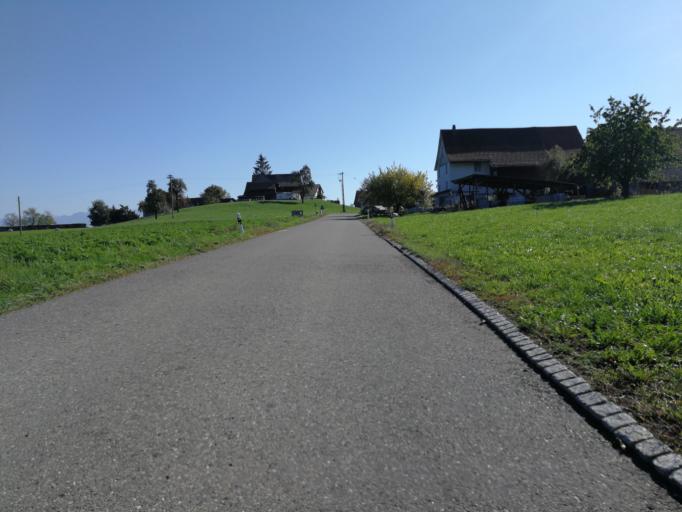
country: CH
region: Zurich
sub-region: Bezirk Uster
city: Hinteregg
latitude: 47.3154
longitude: 8.6758
